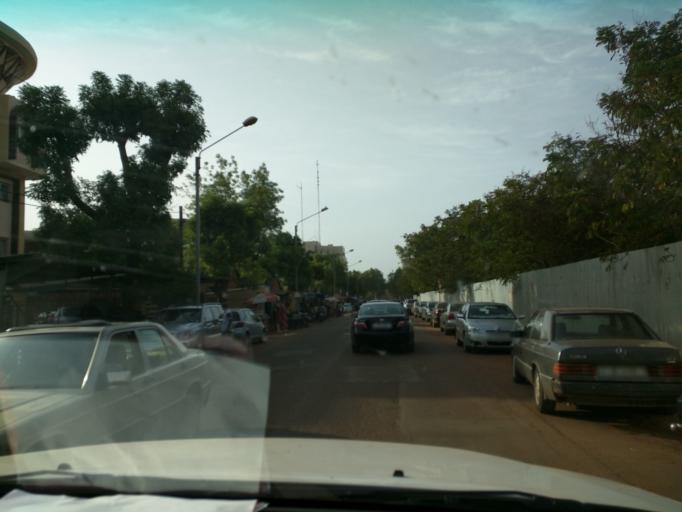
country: BF
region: Centre
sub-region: Kadiogo Province
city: Ouagadougou
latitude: 12.3704
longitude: -1.5158
